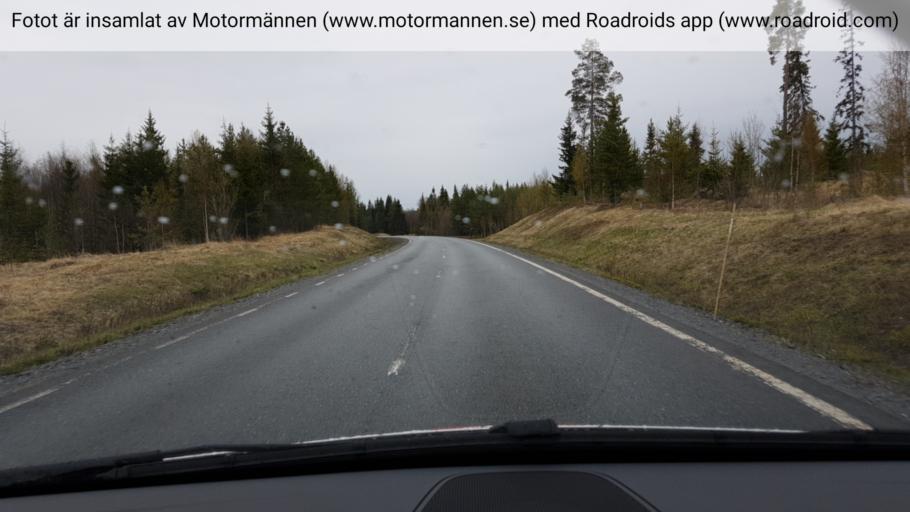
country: SE
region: Jaemtland
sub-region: Krokoms Kommun
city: Krokom
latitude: 63.2965
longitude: 14.4299
